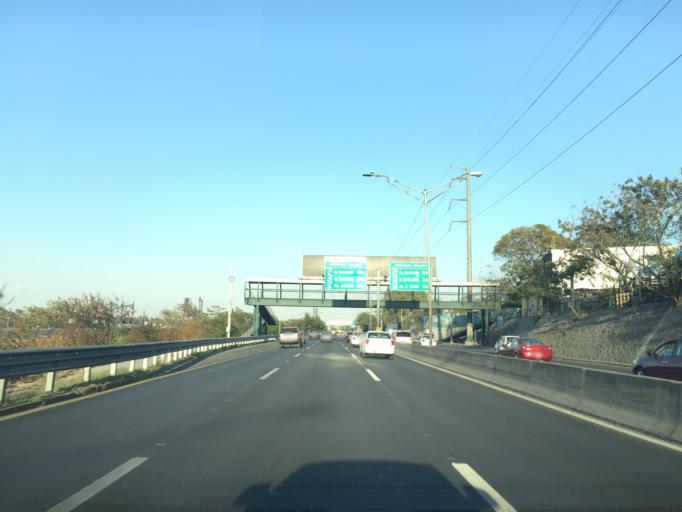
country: MX
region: Nuevo Leon
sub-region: Monterrey
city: Monterrey
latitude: 25.6683
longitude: -100.2942
